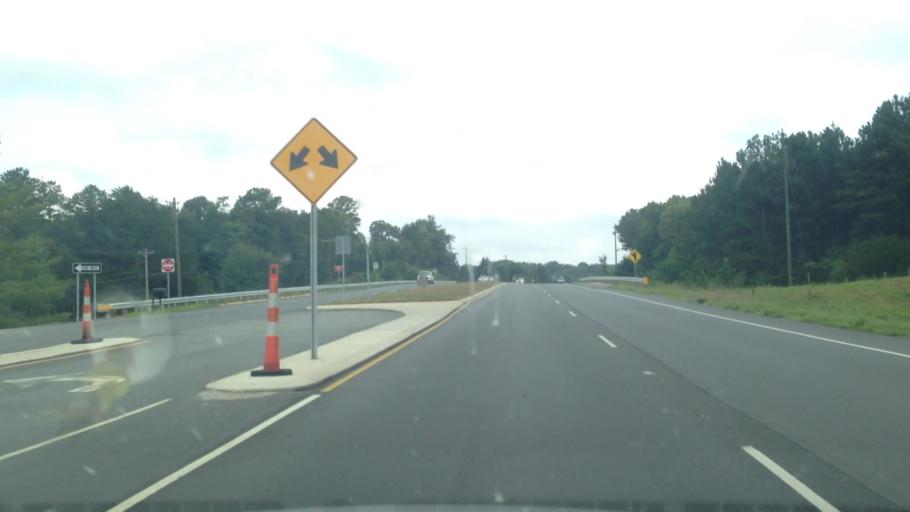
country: US
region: North Carolina
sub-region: Guilford County
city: Summerfield
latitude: 36.1808
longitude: -79.8861
